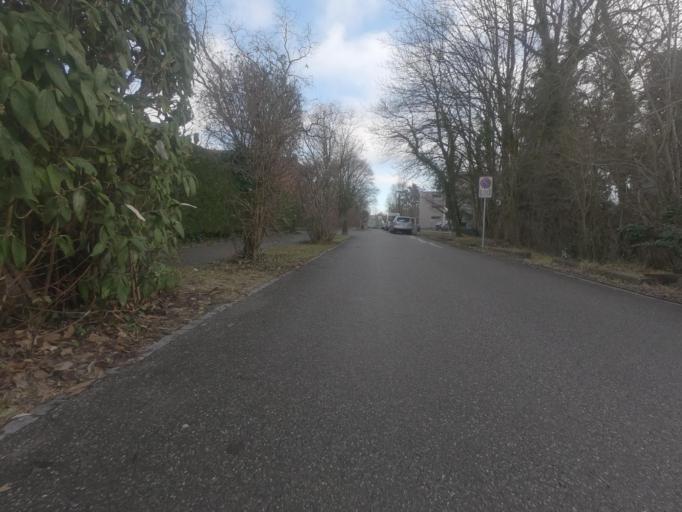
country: CH
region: Solothurn
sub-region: Bezirk Solothurn
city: Solothurn
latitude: 47.2077
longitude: 7.5270
